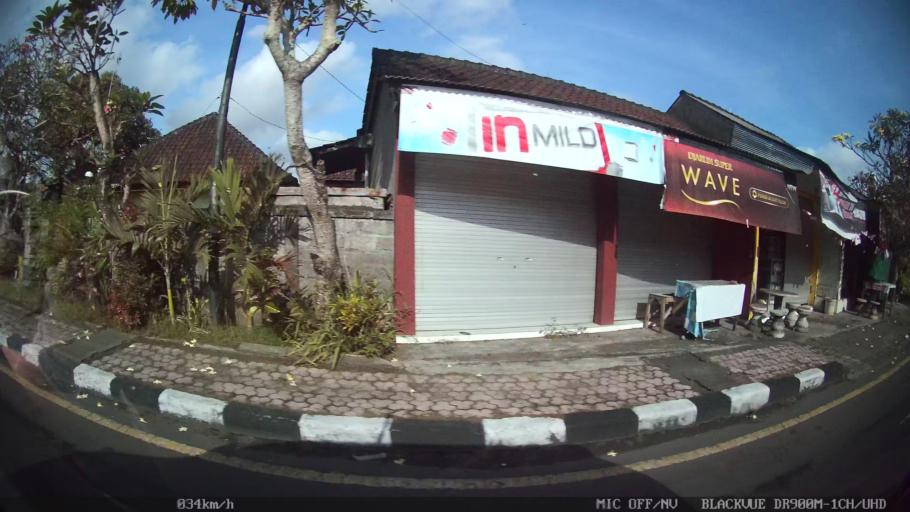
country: ID
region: Bali
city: Banjar Jumbayah
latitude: -8.5625
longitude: 115.1708
